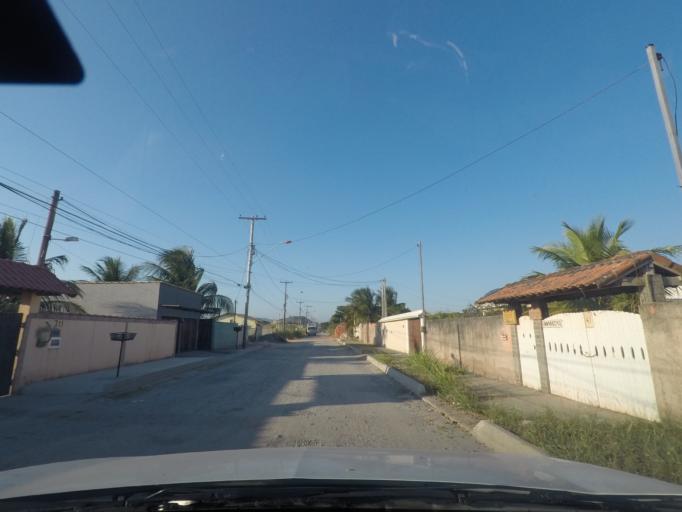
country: BR
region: Rio de Janeiro
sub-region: Marica
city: Marica
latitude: -22.9641
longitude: -42.9334
